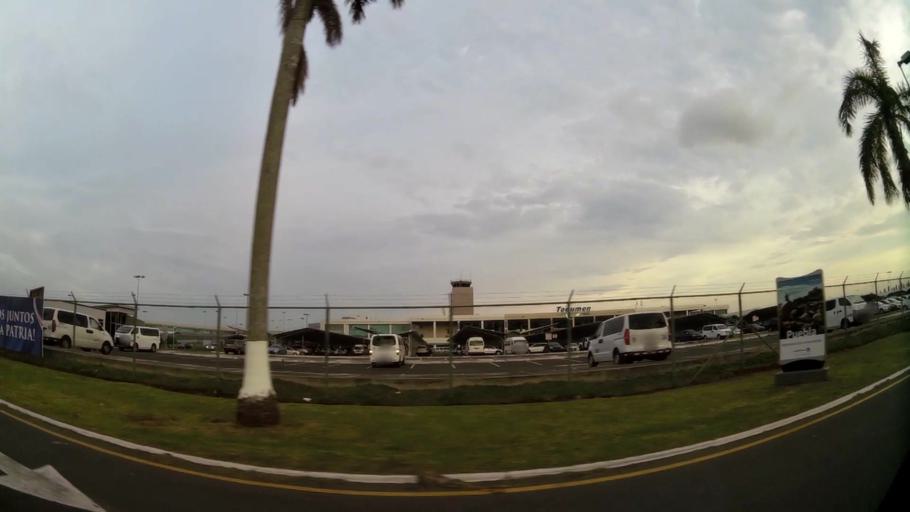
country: PA
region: Panama
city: Tocumen
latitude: 9.0684
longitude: -79.3887
